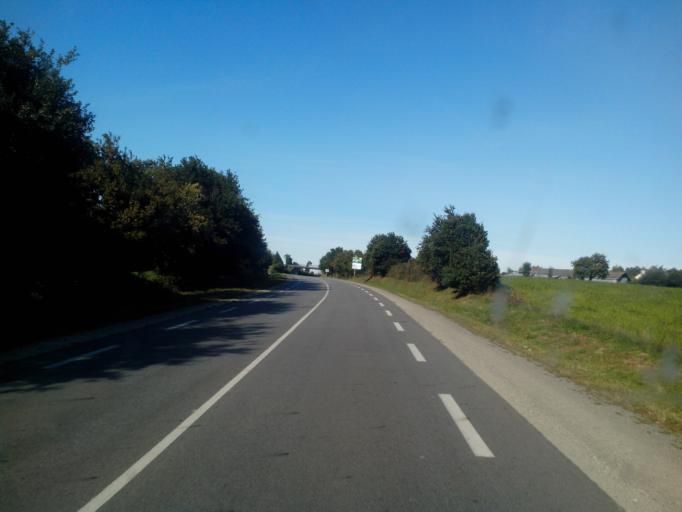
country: FR
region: Brittany
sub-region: Departement du Morbihan
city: Loyat
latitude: 47.9800
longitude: -2.3741
